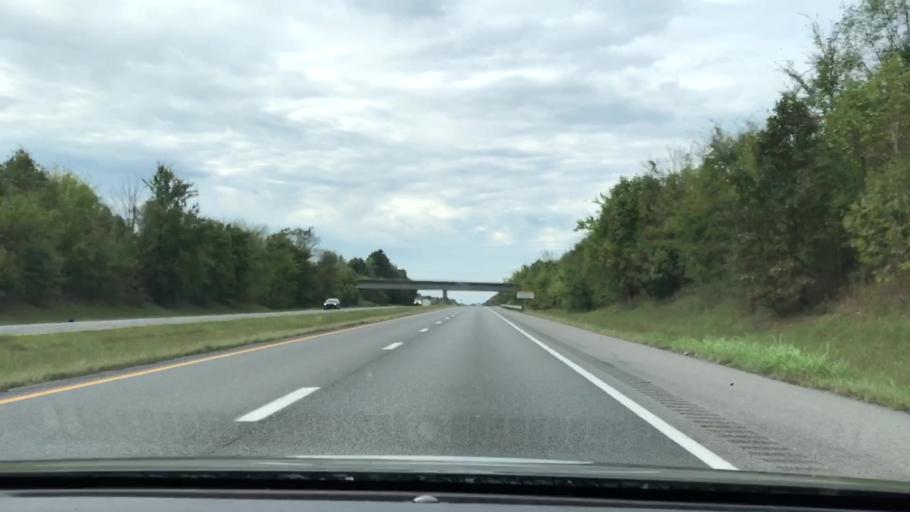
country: US
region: Kentucky
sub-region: Marshall County
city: Calvert City
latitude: 36.9704
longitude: -88.3470
